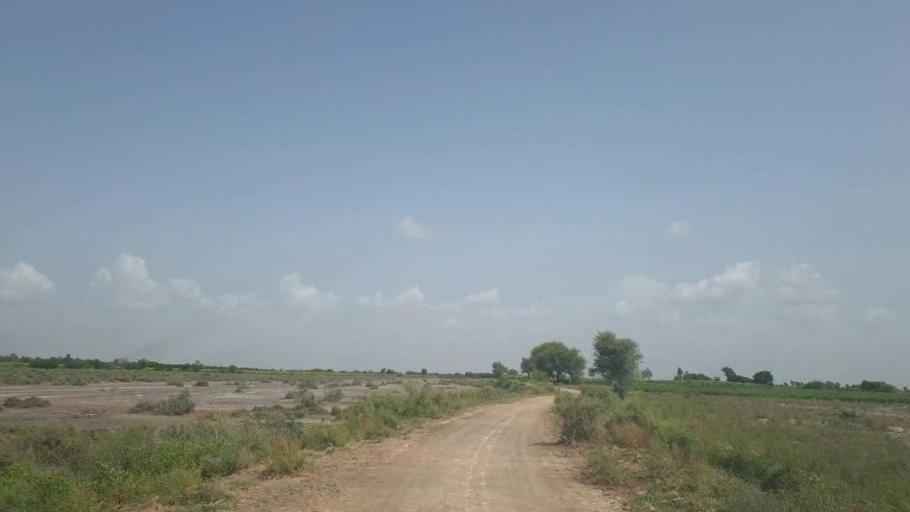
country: PK
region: Sindh
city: Tando Bago
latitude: 24.7525
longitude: 69.1755
